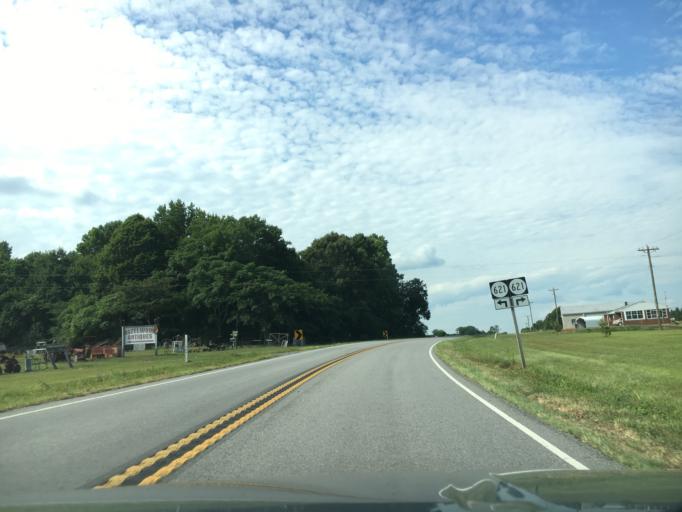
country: US
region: Virginia
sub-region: Halifax County
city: Mountain Road
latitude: 36.9035
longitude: -79.0182
